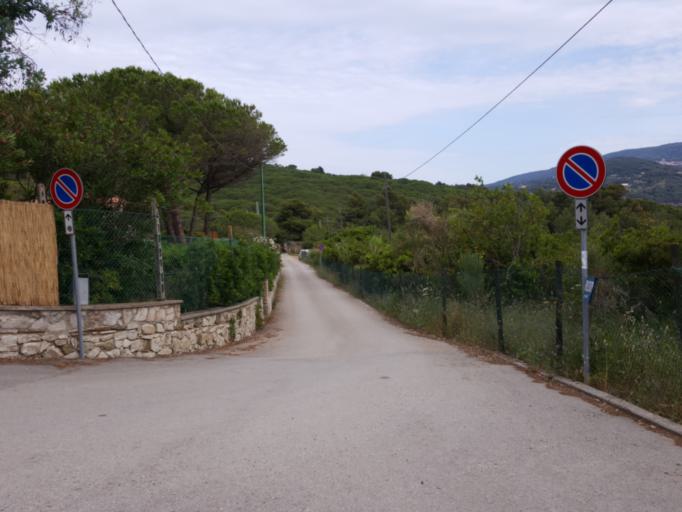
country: IT
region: Tuscany
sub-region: Provincia di Livorno
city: Capoliveri
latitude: 42.7653
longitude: 10.3415
